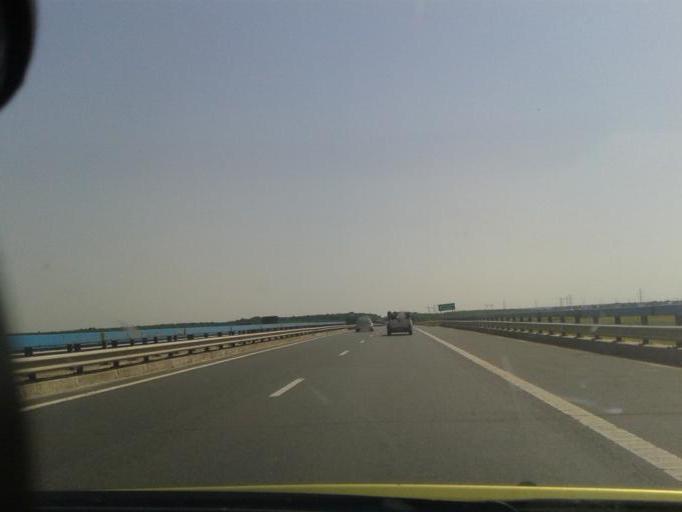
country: RO
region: Ilfov
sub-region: Comuna Cernica
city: Cernica
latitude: 44.4099
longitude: 26.2826
